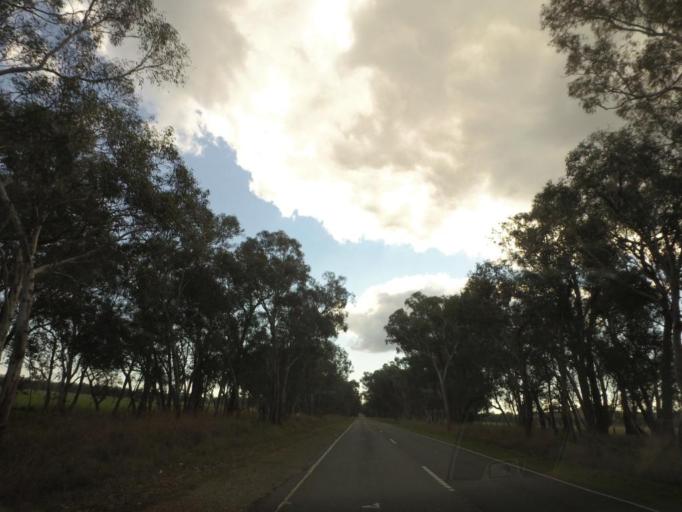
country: AU
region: New South Wales
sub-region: Corowa Shire
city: Howlong
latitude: -36.1928
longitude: 146.6157
